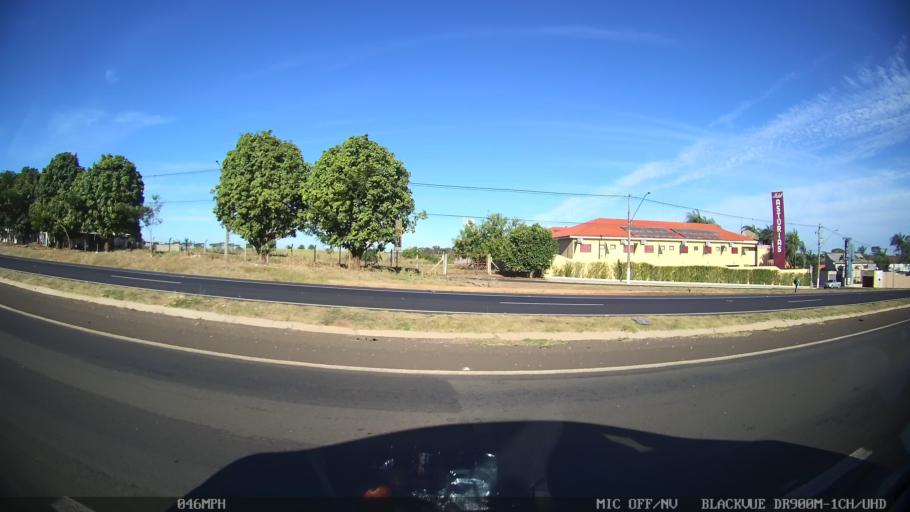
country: BR
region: Sao Paulo
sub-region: Bady Bassitt
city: Bady Bassitt
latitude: -20.8764
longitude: -49.4197
